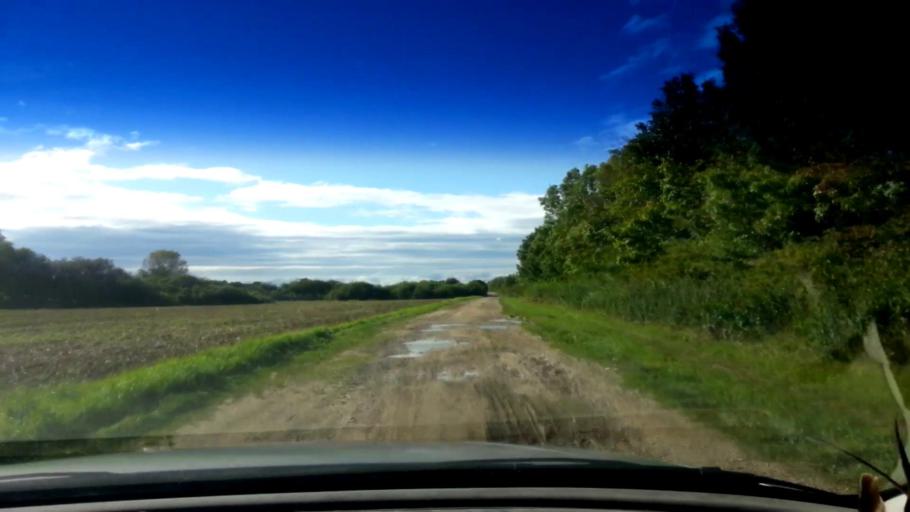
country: DE
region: Bavaria
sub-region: Upper Franconia
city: Bischberg
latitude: 49.9203
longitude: 10.8332
